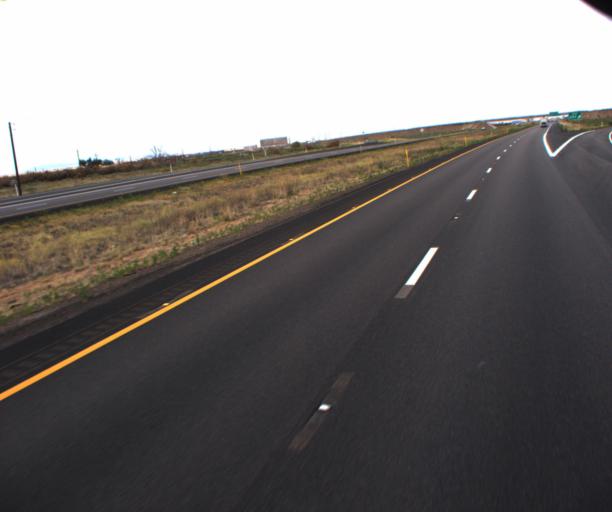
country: US
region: Arizona
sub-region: Navajo County
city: Winslow
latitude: 35.0075
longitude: -110.6357
